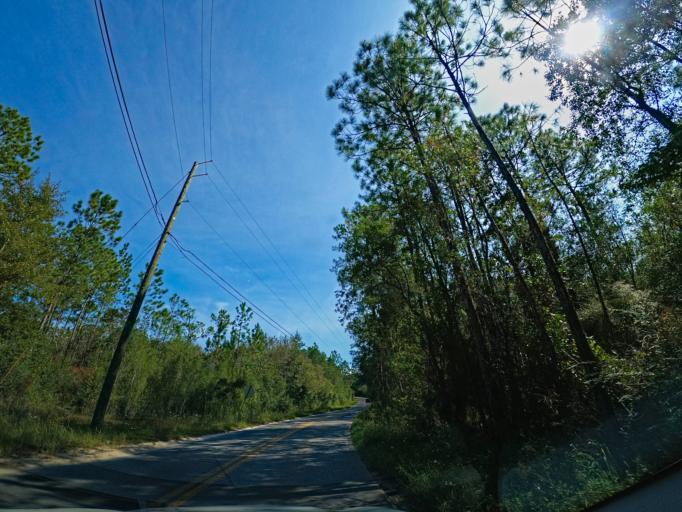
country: US
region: Florida
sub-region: Okaloosa County
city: Crestview
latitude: 30.7079
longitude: -86.5968
